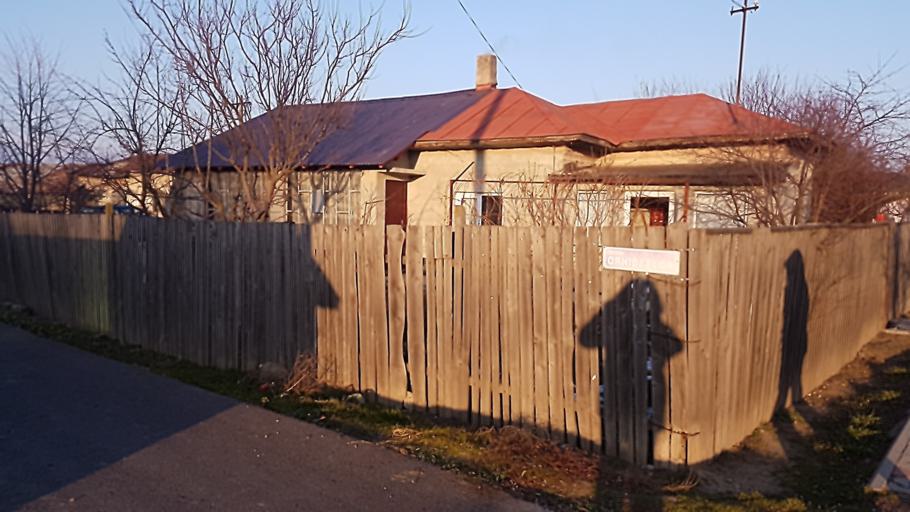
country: RO
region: Giurgiu
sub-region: Comuna Hotarele
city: Hotarele
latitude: 44.1753
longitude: 26.3592
